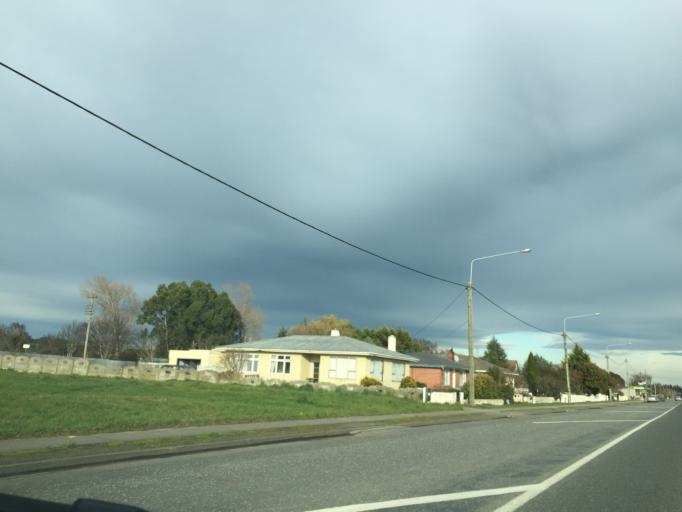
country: NZ
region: Southland
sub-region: Gore District
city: Gore
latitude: -46.1958
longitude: 168.8625
